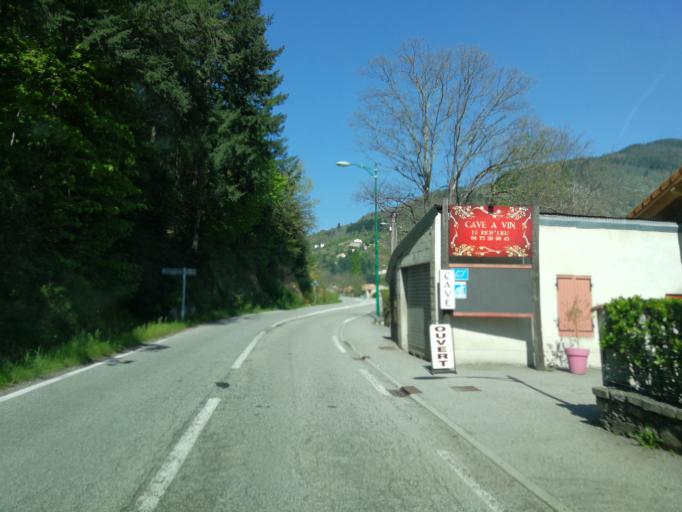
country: FR
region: Rhone-Alpes
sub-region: Departement de l'Ardeche
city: Le Cheylard
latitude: 44.9122
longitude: 4.4390
